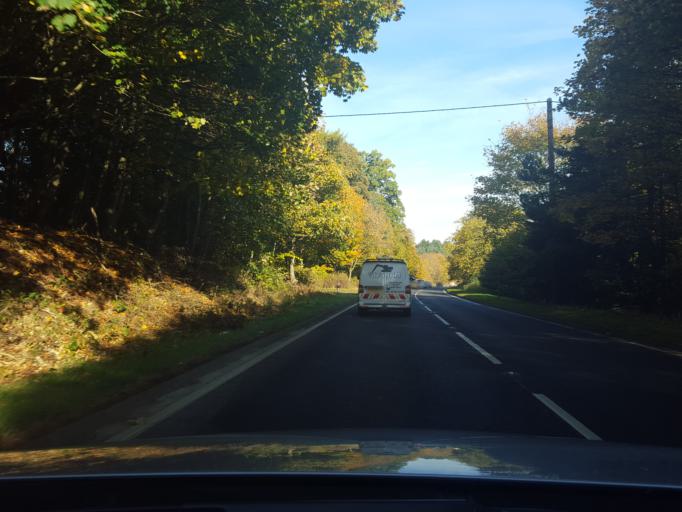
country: GB
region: Scotland
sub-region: Highland
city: Inverness
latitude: 57.4548
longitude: -4.2753
